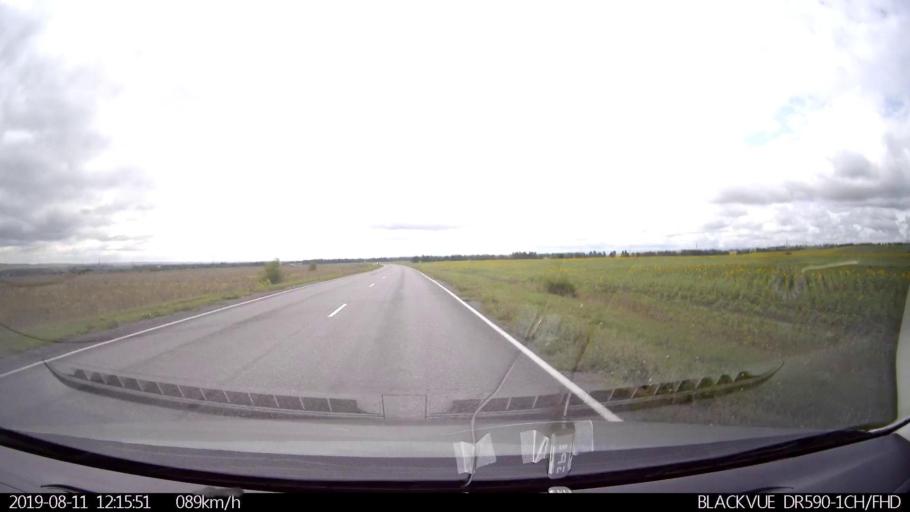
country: RU
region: Ulyanovsk
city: Ignatovka
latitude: 53.9371
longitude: 47.9643
